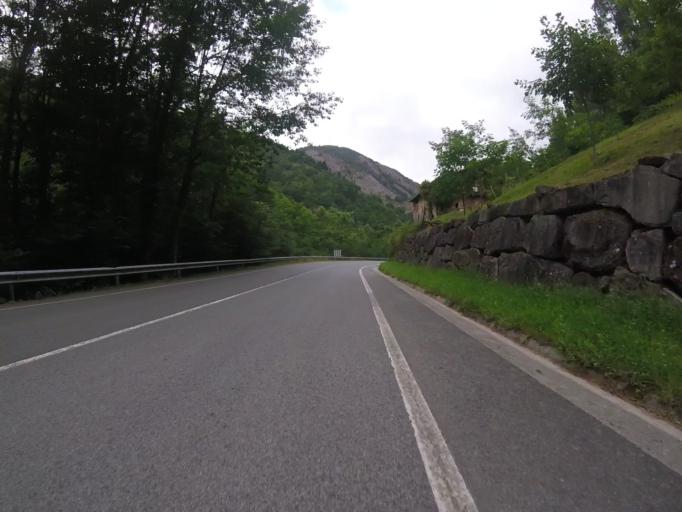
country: ES
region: Navarre
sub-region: Provincia de Navarra
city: Saldias
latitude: 43.1055
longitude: -1.7670
